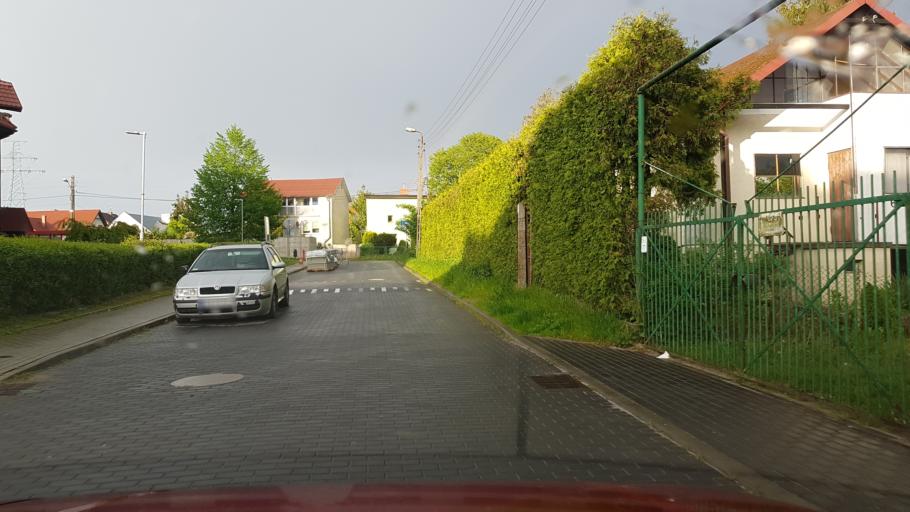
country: PL
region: West Pomeranian Voivodeship
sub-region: Szczecin
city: Szczecin
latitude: 53.4688
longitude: 14.5487
